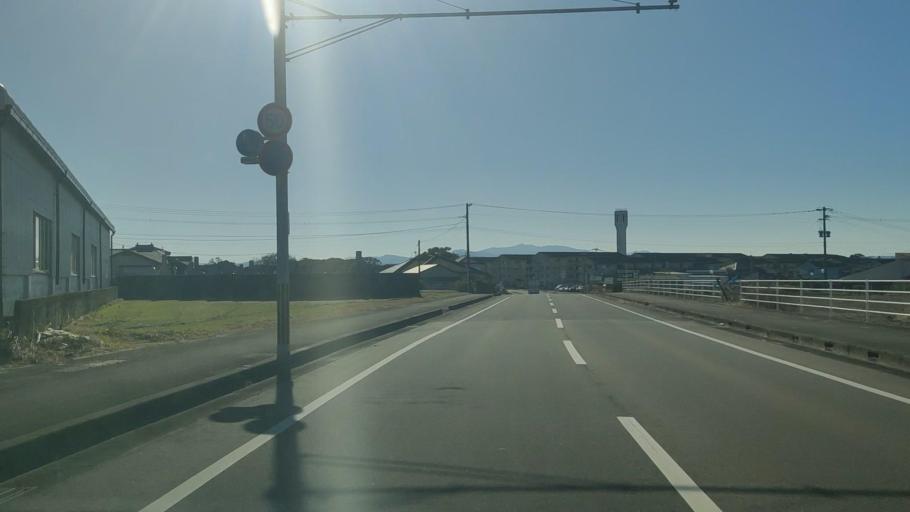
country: JP
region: Miyazaki
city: Miyazaki-shi
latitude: 31.9549
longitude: 131.4625
